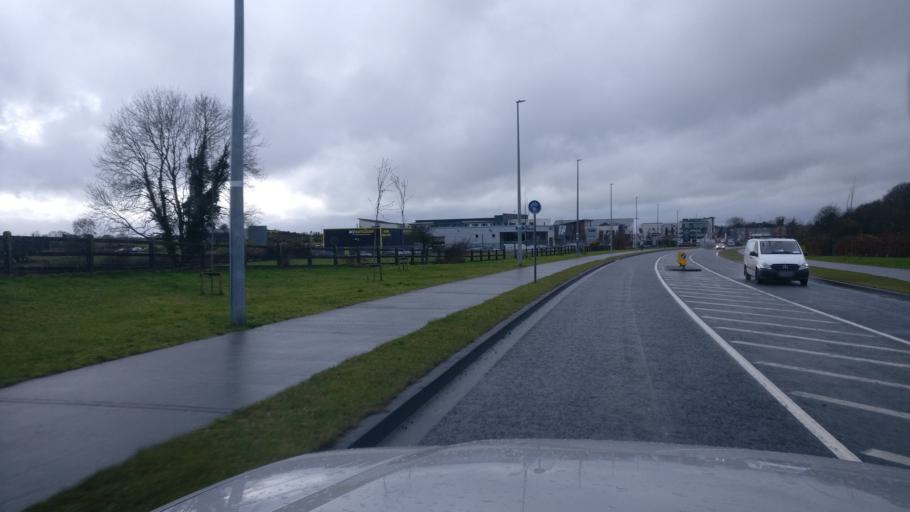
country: IE
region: Leinster
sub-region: An Iarmhi
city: Athlone
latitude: 53.4210
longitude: -7.9925
